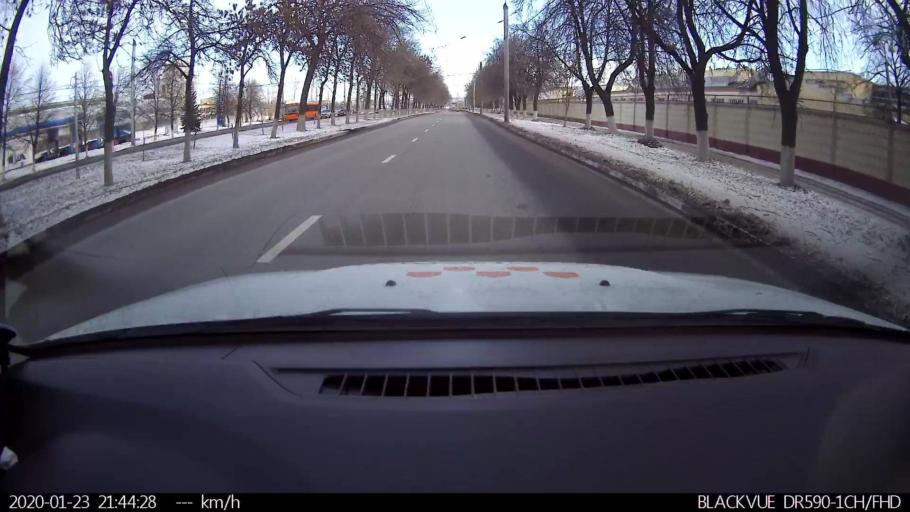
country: RU
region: Nizjnij Novgorod
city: Nizhniy Novgorod
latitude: 56.2561
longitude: 43.8976
